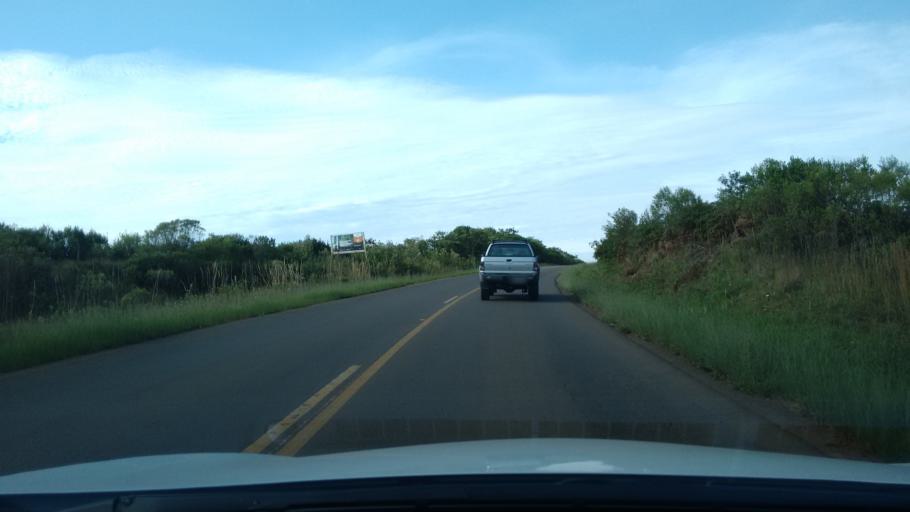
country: BR
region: Santa Catarina
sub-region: Videira
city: Videira
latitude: -27.0774
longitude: -50.8993
